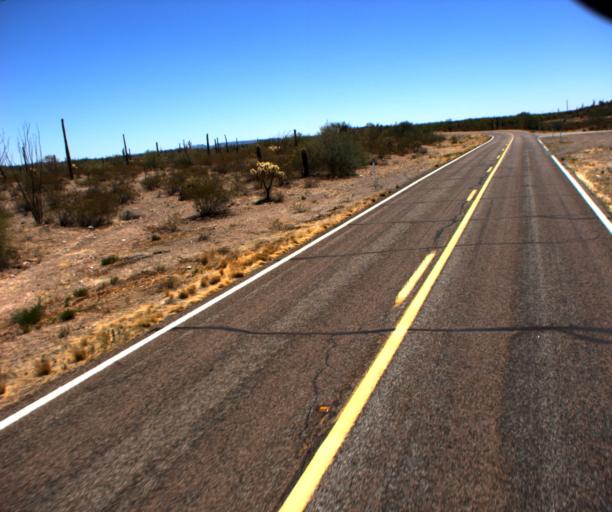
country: US
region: Arizona
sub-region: Pima County
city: Ajo
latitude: 32.2223
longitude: -112.6884
